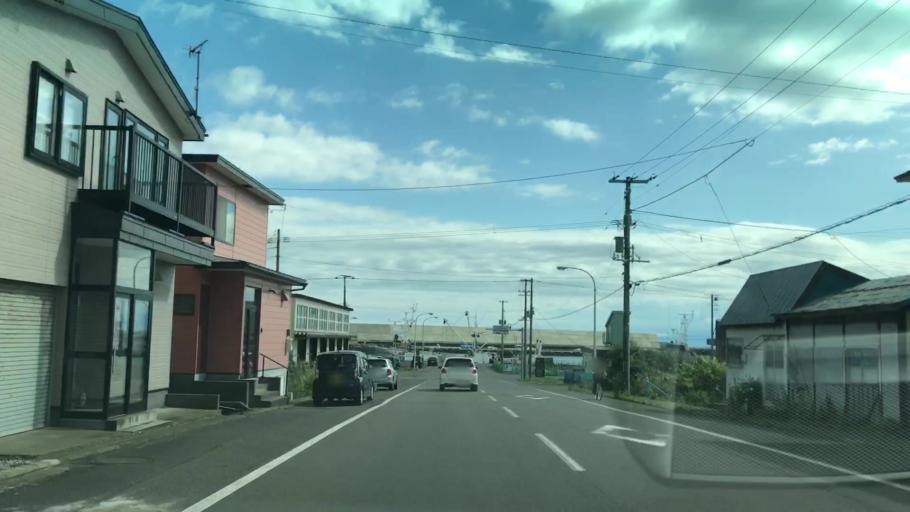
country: JP
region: Hokkaido
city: Muroran
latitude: 42.3102
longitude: 140.9730
